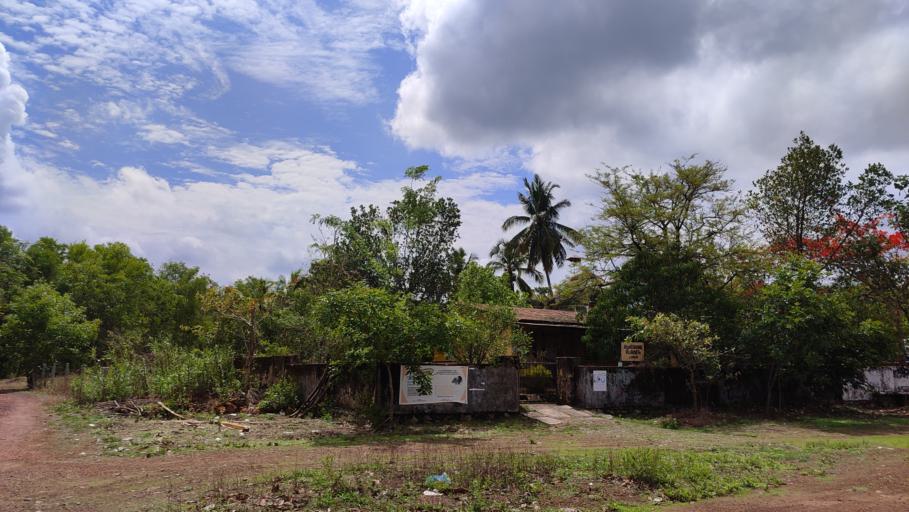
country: IN
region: Kerala
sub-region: Kasaragod District
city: Kannangad
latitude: 12.3839
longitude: 75.1008
